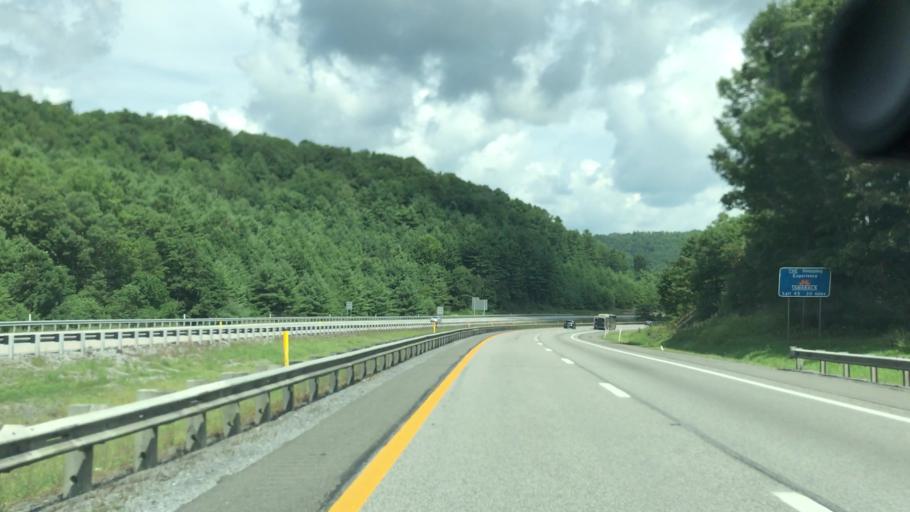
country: US
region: West Virginia
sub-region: Mercer County
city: Athens
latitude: 37.4428
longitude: -81.0653
